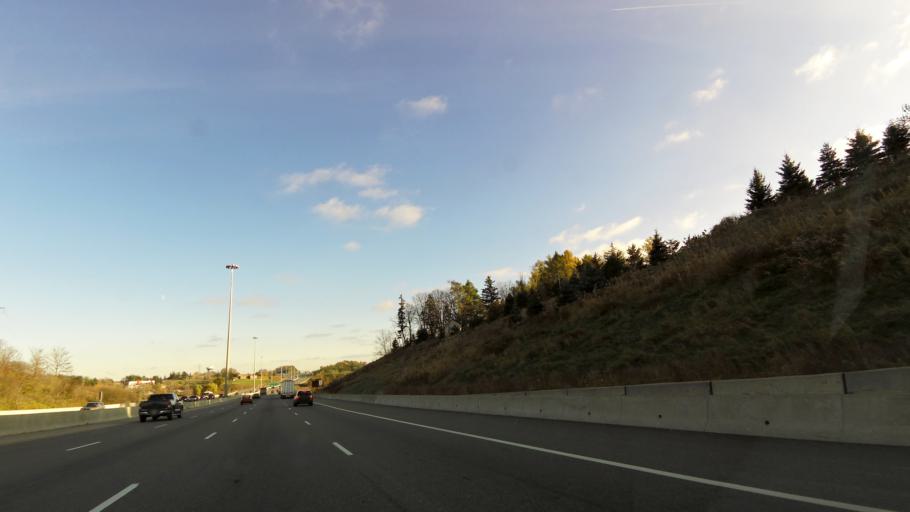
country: CA
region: Ontario
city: Kitchener
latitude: 43.4216
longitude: -80.4198
